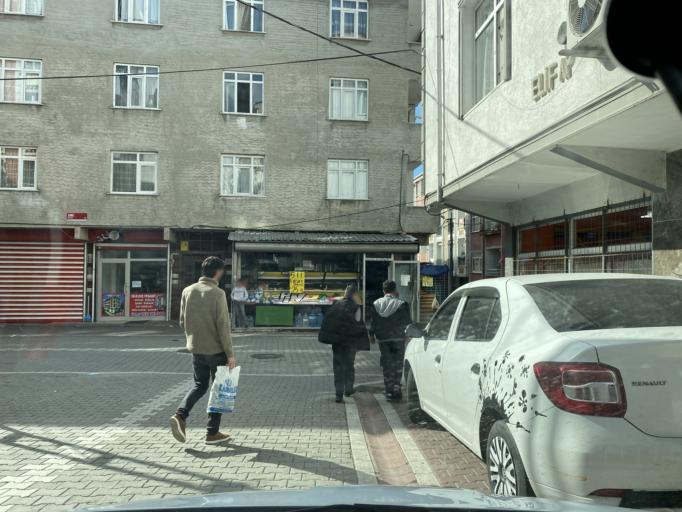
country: TR
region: Istanbul
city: Esenyurt
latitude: 41.0313
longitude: 28.6668
